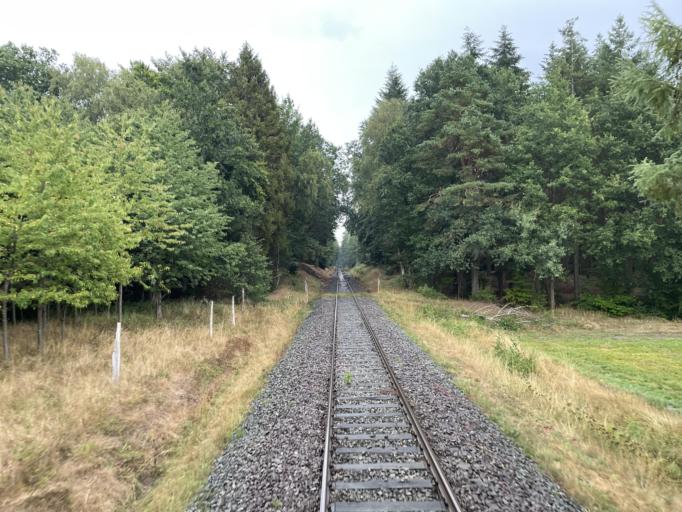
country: DE
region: Lower Saxony
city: Betzendorf
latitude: 53.1504
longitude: 10.3276
